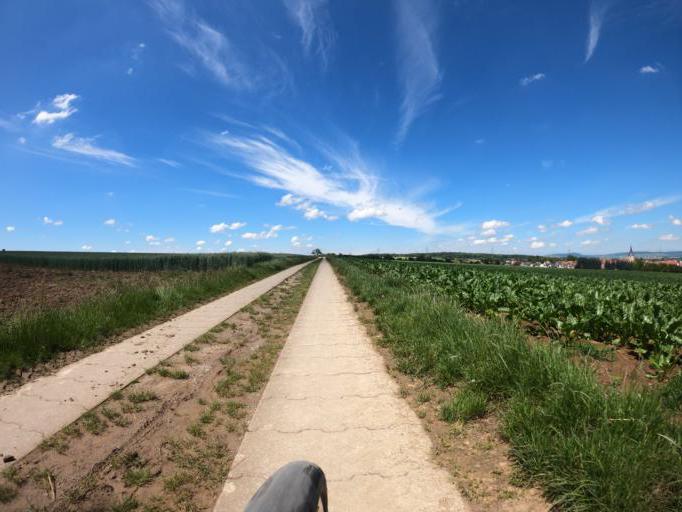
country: DE
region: Baden-Wuerttemberg
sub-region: Regierungsbezirk Stuttgart
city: Tamm
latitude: 48.9158
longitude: 9.1203
